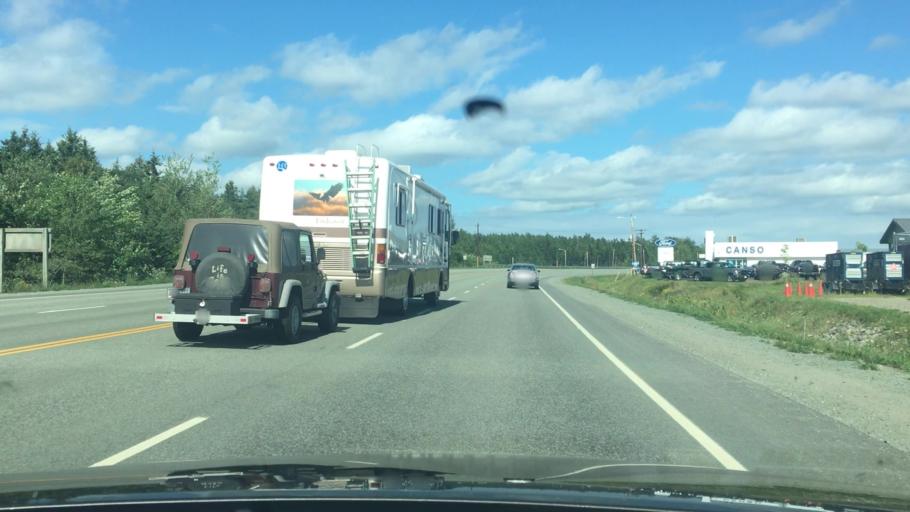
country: CA
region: Nova Scotia
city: Port Hawkesbury
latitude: 45.6136
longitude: -61.3427
